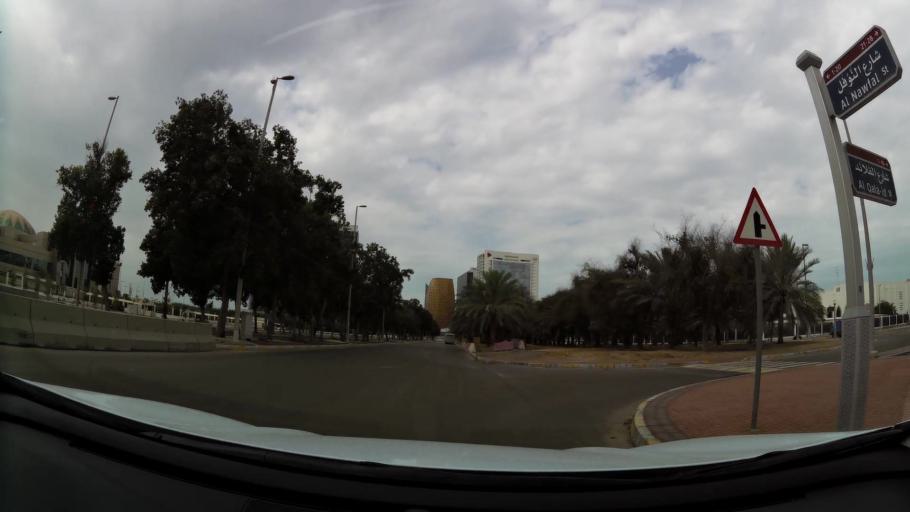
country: AE
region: Abu Dhabi
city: Abu Dhabi
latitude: 24.4182
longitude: 54.4476
